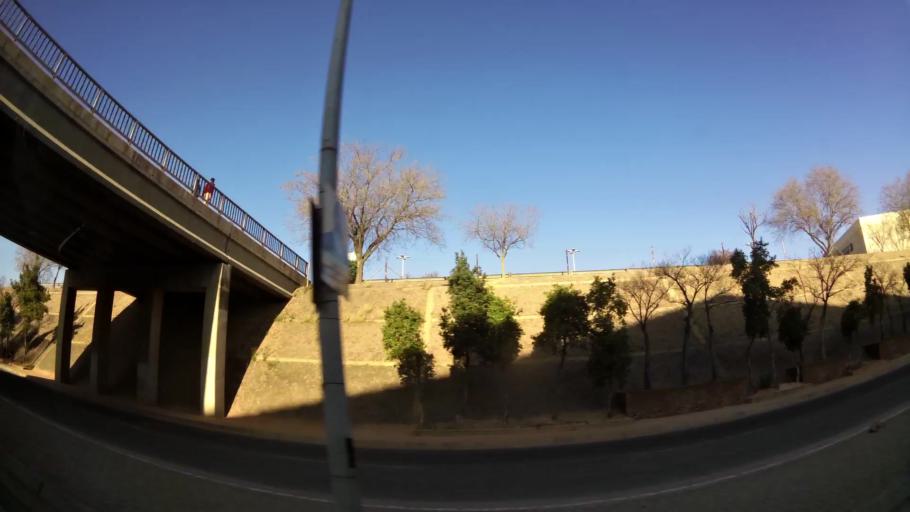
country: ZA
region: Gauteng
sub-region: City of Johannesburg Metropolitan Municipality
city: Roodepoort
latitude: -26.1379
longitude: 27.8614
